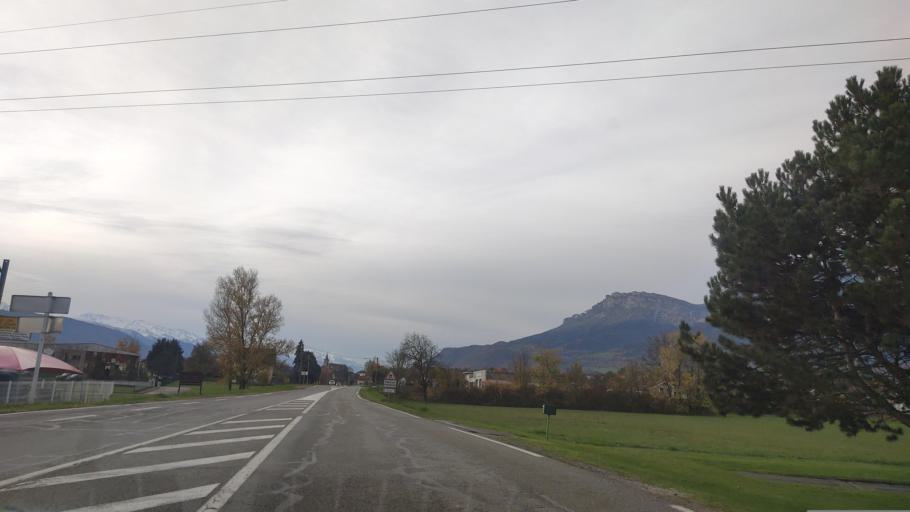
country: FR
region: Rhone-Alpes
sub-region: Departement de la Savoie
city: Les Marches
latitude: 45.5073
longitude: 6.0031
